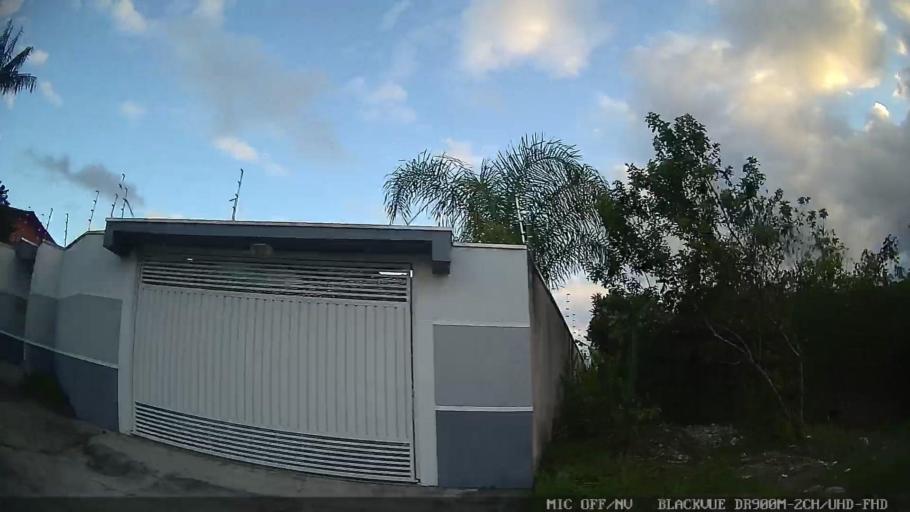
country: BR
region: Sao Paulo
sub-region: Caraguatatuba
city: Caraguatatuba
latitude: -23.6632
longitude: -45.4438
